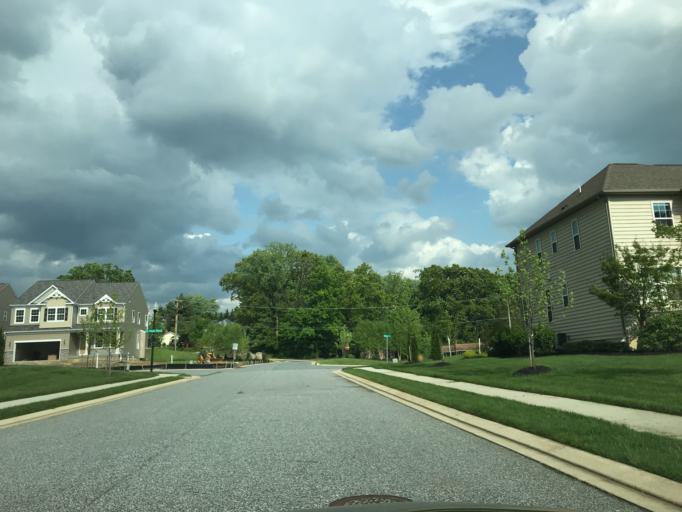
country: US
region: Maryland
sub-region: Harford County
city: Bel Air North
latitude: 39.5520
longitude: -76.3798
